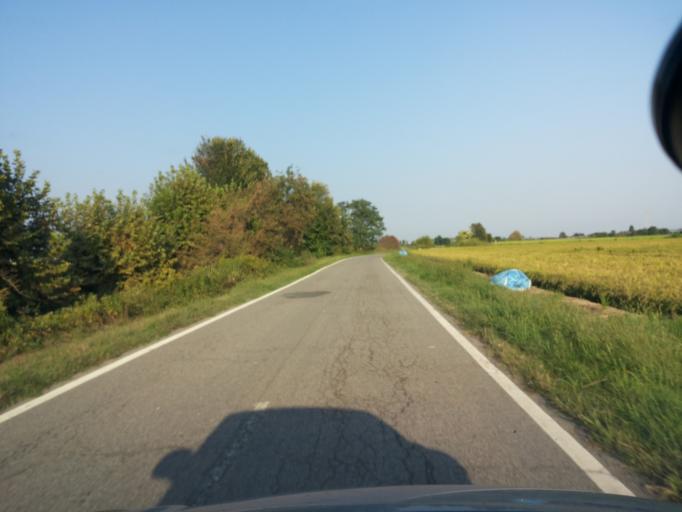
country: IT
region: Piedmont
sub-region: Provincia di Vercelli
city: Sali Vercellese
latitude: 45.3050
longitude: 8.3415
